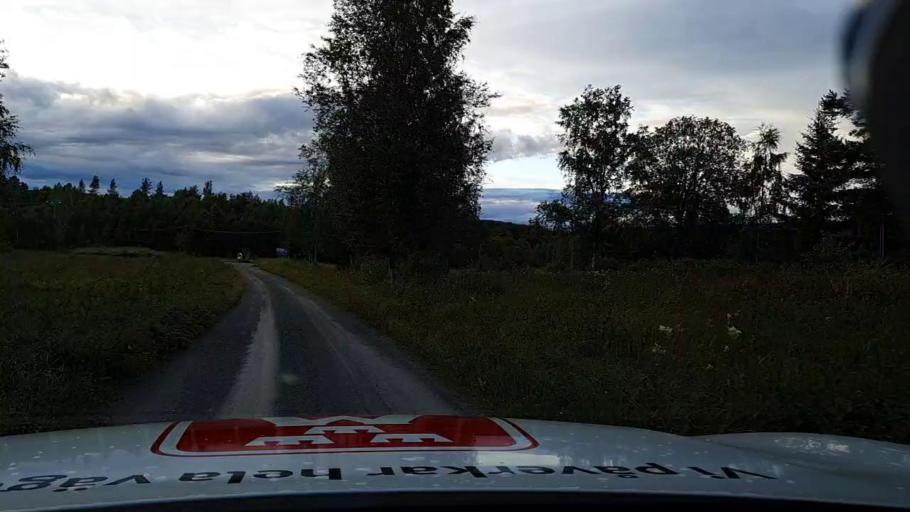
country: SE
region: Jaemtland
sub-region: Bergs Kommun
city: Hoverberg
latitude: 62.8717
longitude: 14.6219
